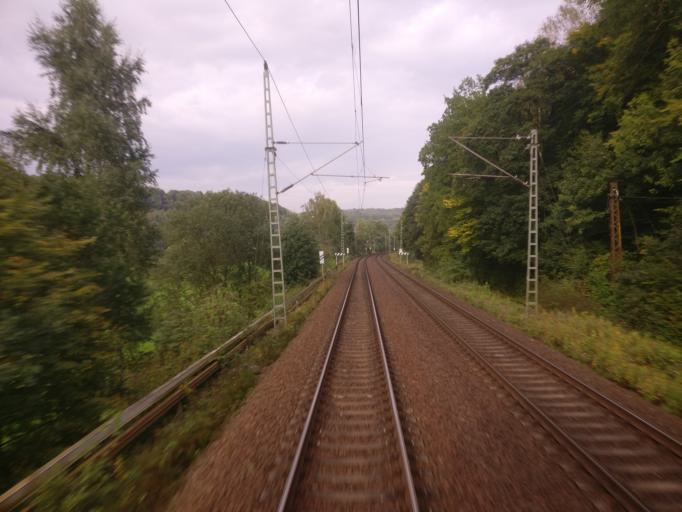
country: DE
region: Saxony
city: Struppen
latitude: 50.9487
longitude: 14.0180
